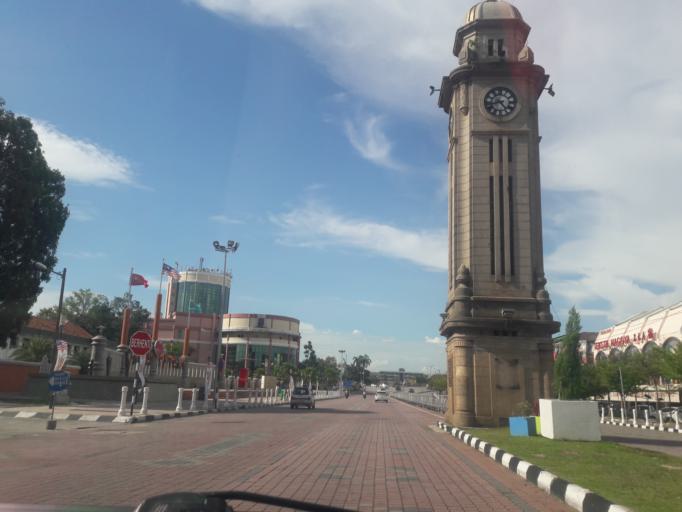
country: MY
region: Kedah
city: Sungai Petani
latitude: 5.6432
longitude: 100.4890
